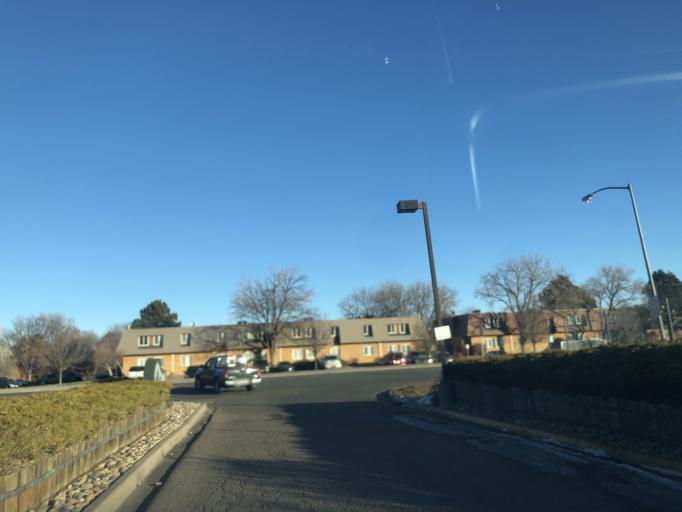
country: US
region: Colorado
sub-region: Adams County
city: Aurora
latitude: 39.7177
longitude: -104.8198
